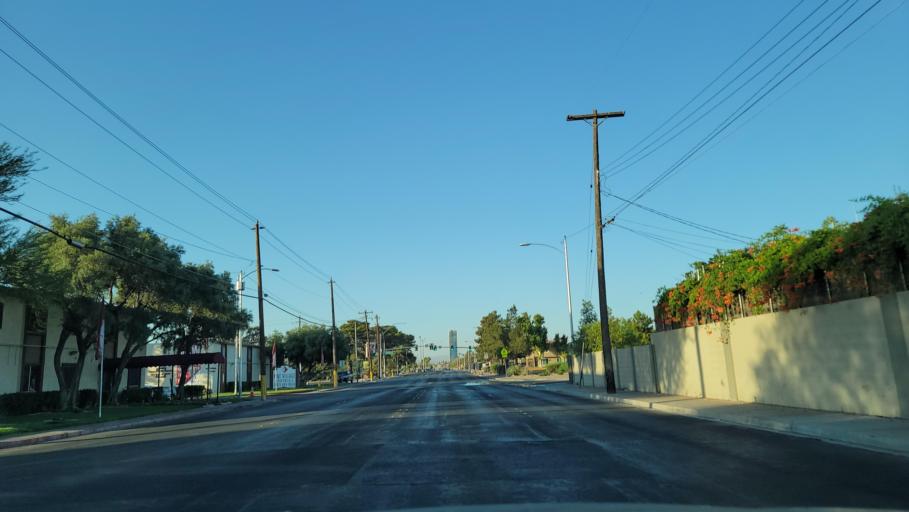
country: US
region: Nevada
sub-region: Clark County
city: Spring Valley
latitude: 36.1388
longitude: -115.1996
